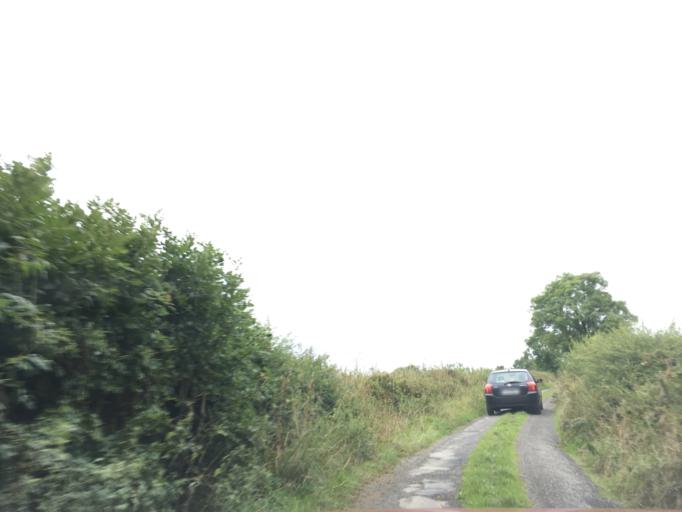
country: IE
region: Munster
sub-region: An Clar
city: Ennis
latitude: 52.7239
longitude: -9.0945
